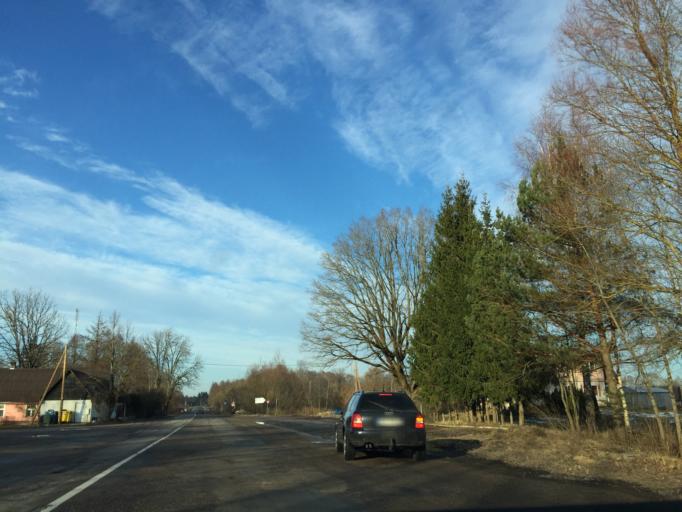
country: LV
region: Kekava
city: Balozi
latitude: 56.7657
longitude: 24.1084
